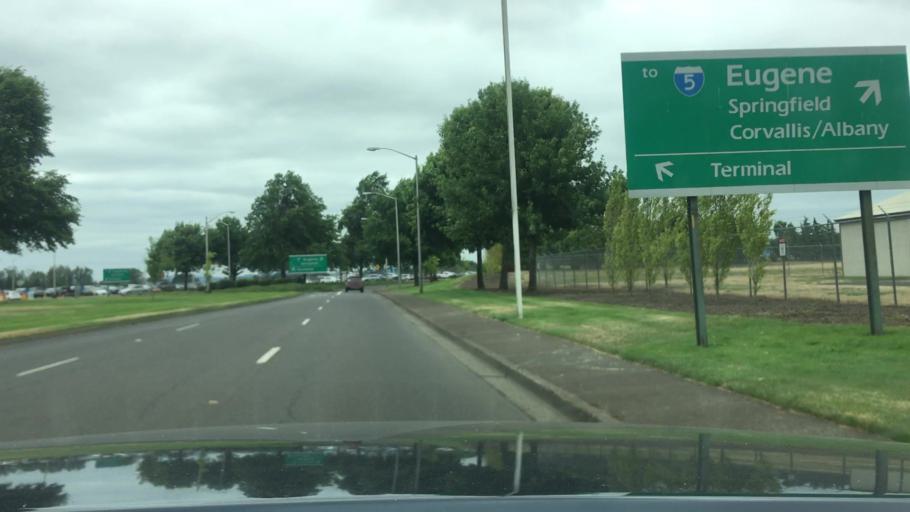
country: US
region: Oregon
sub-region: Lane County
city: Junction City
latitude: 44.1165
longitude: -123.2099
